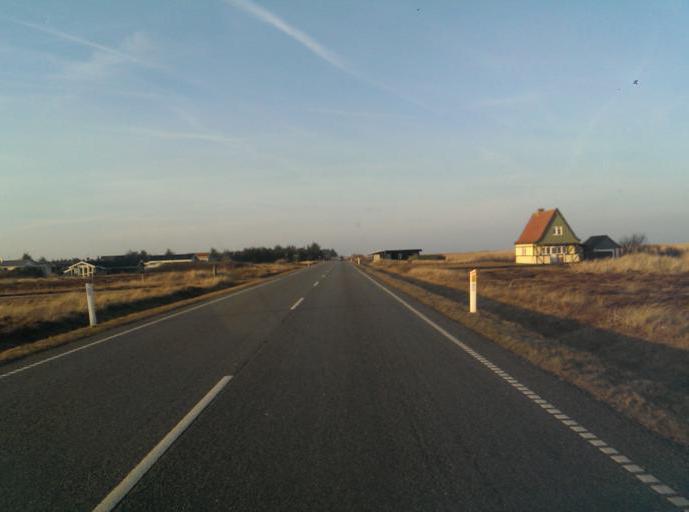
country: DK
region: Central Jutland
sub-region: Ringkobing-Skjern Kommune
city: Hvide Sande
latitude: 55.8457
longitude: 8.1744
